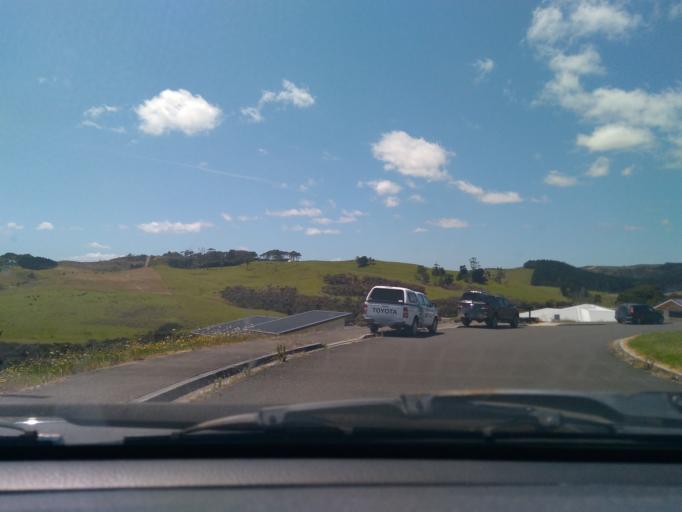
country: NZ
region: Northland
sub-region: Far North District
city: Taipa
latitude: -34.9943
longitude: 173.5108
